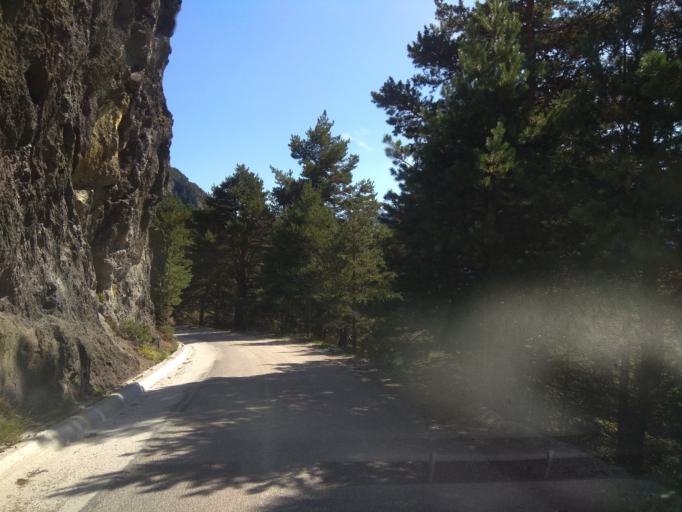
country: ES
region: Catalonia
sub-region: Provincia de Lleida
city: Les
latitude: 42.7674
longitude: 0.7132
